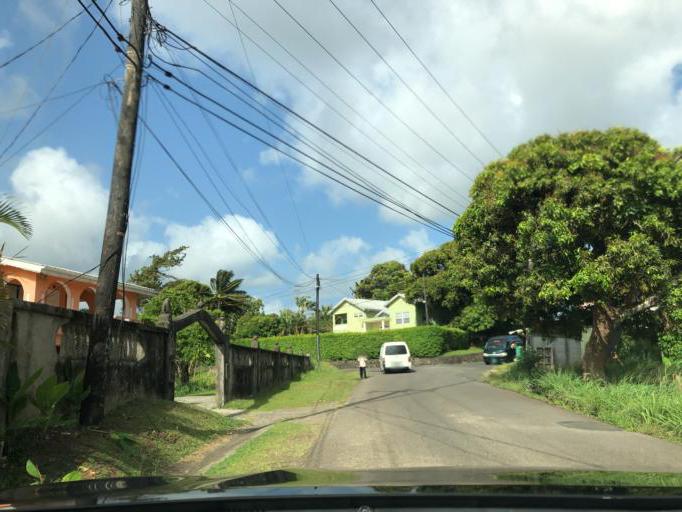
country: LC
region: Castries Quarter
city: Bisee
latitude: 13.9959
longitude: -60.9543
